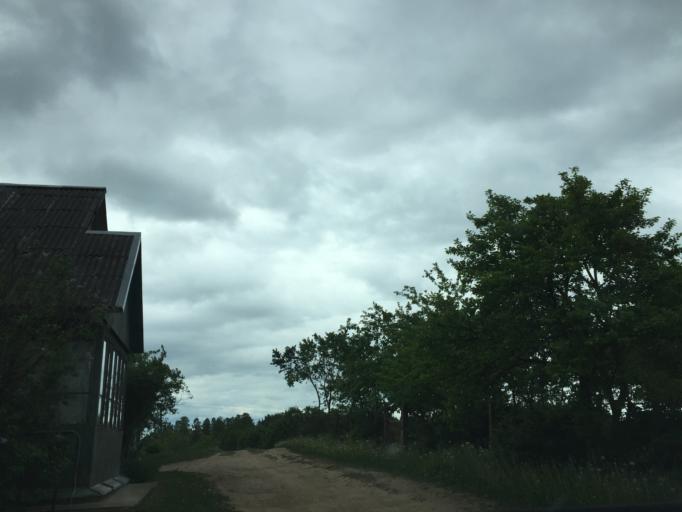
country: LV
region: Dagda
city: Dagda
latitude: 56.1876
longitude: 27.6459
